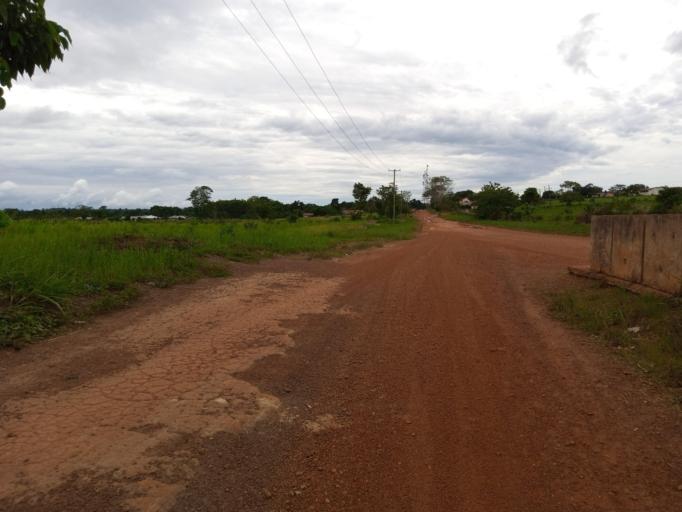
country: SL
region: Southern Province
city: Largo
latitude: 8.1143
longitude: -12.0644
